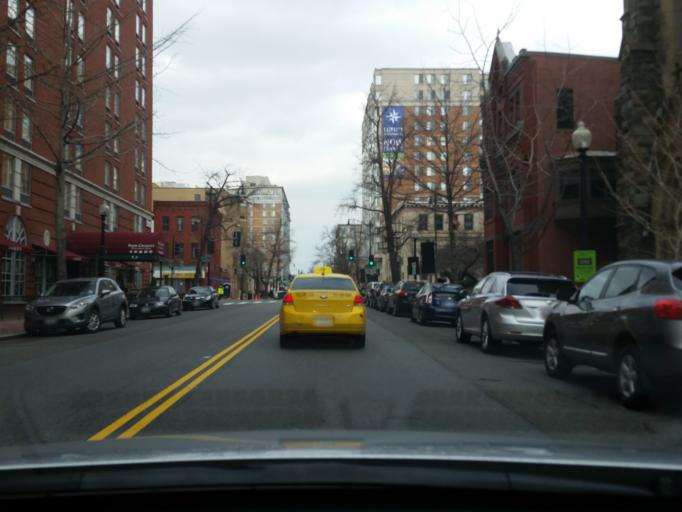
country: US
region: Washington, D.C.
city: Washington, D.C.
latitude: 38.8991
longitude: -77.0189
